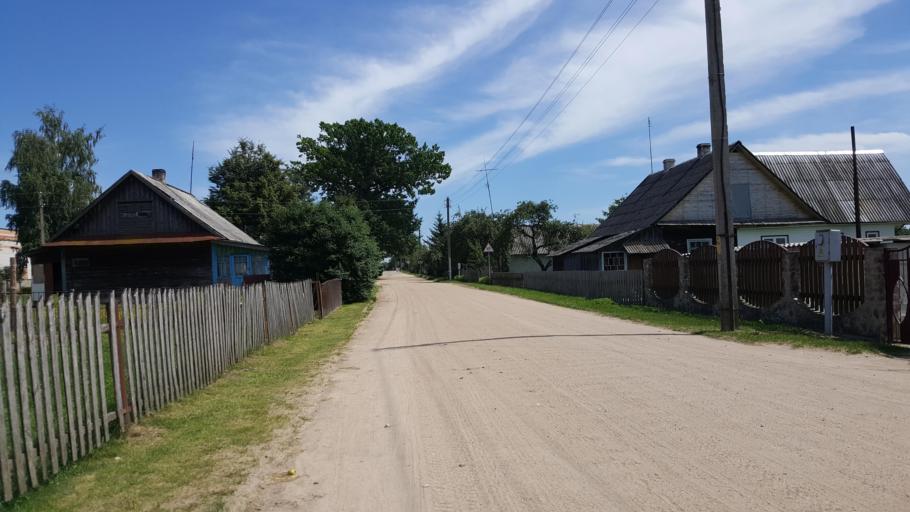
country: BY
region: Brest
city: Pruzhany
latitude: 52.5612
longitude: 24.2108
